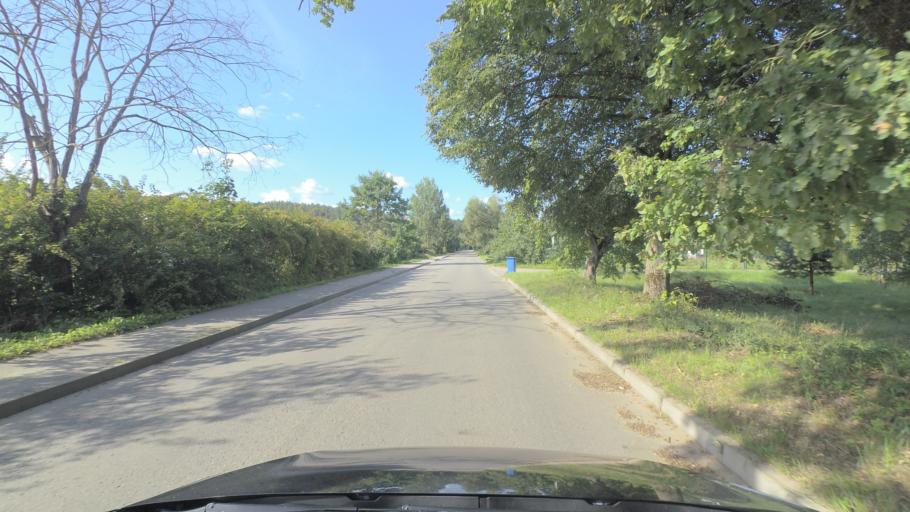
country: LT
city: Nemencine
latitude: 54.8386
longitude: 25.3708
